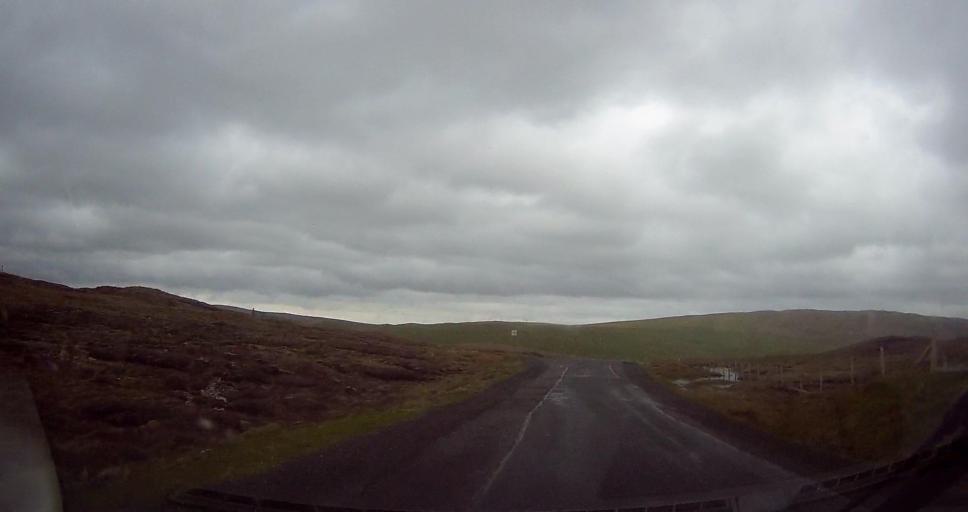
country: GB
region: Scotland
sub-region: Shetland Islands
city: Lerwick
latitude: 60.4800
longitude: -1.4164
